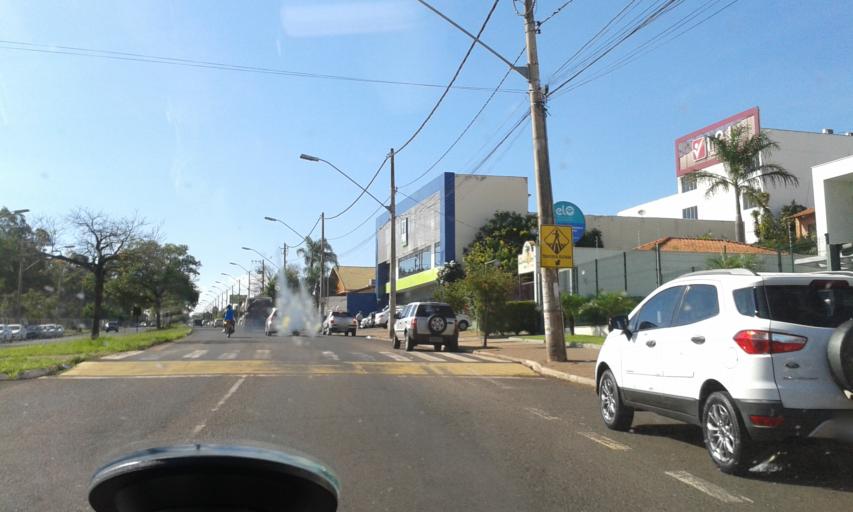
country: BR
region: Minas Gerais
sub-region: Uberlandia
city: Uberlandia
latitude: -18.9114
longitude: -48.2430
